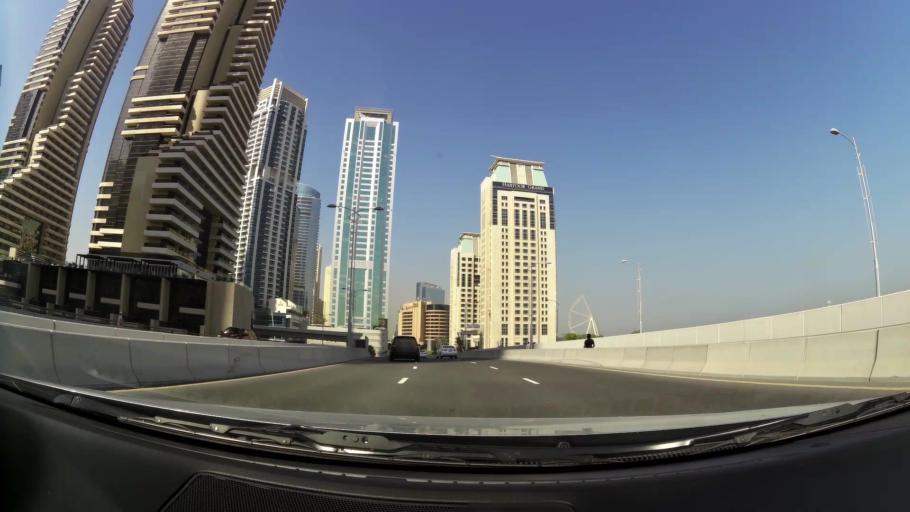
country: AE
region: Dubai
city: Dubai
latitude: 25.0874
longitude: 55.1436
